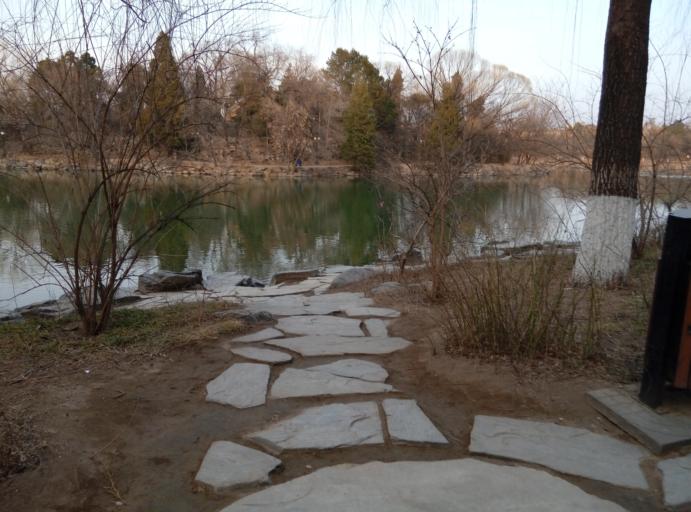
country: CN
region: Beijing
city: Haidian
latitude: 39.9929
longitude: 116.3023
